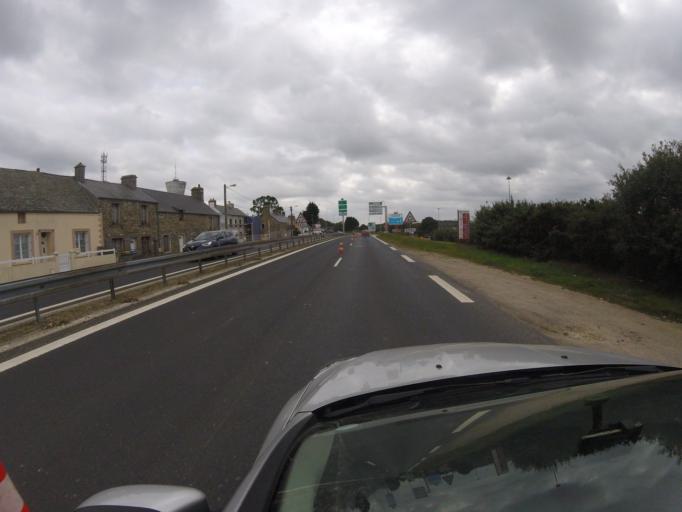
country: FR
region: Lower Normandy
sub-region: Departement de la Manche
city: La Glacerie
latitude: 49.6023
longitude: -1.5982
